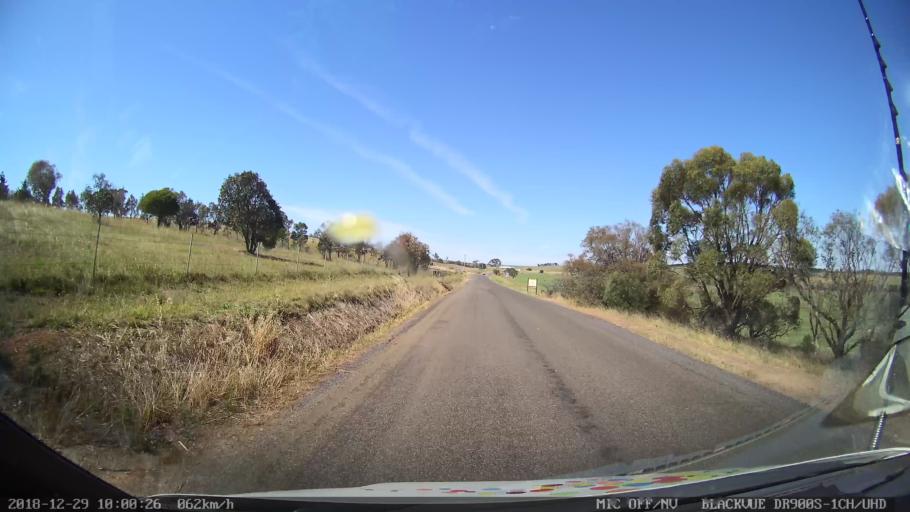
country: AU
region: New South Wales
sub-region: Goulburn Mulwaree
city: Goulburn
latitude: -34.7921
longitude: 149.4855
